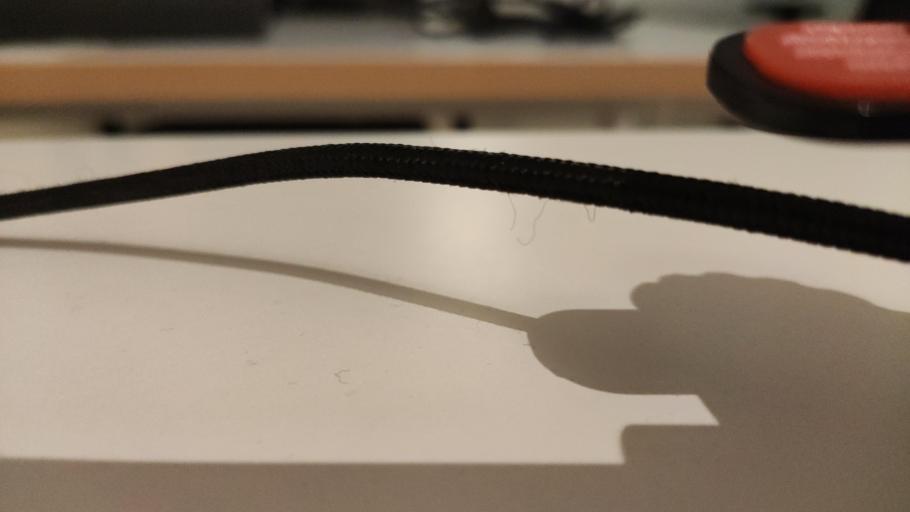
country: RU
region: Moskovskaya
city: Il'inskiy Pogost
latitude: 55.4919
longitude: 38.8738
